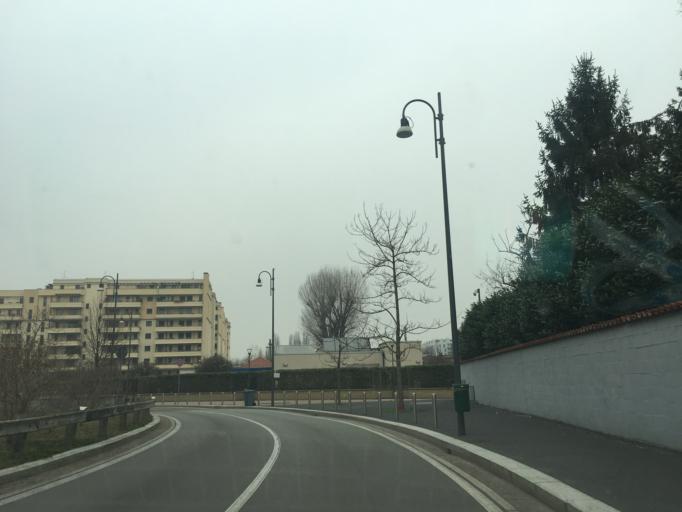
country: IT
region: Lombardy
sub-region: Citta metropolitana di Milano
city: Cesano Boscone
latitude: 45.4704
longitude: 9.1045
